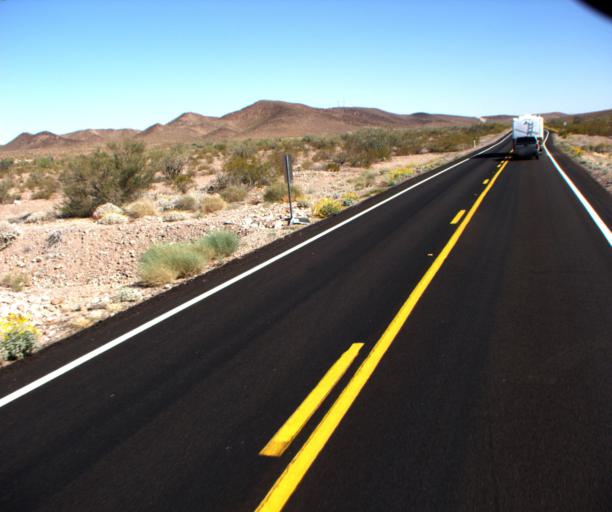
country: US
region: Arizona
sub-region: La Paz County
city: Quartzsite
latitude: 33.2178
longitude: -114.2601
